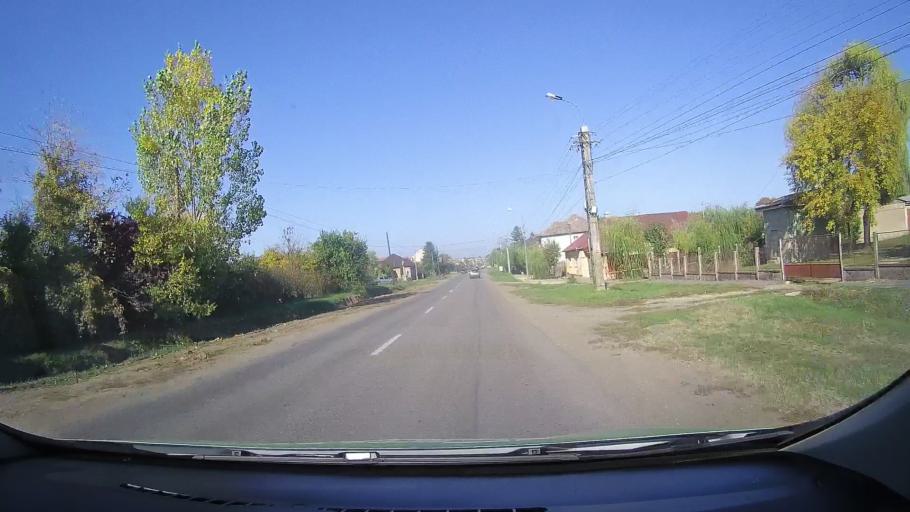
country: RO
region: Satu Mare
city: Carei
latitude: 47.6758
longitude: 22.4786
